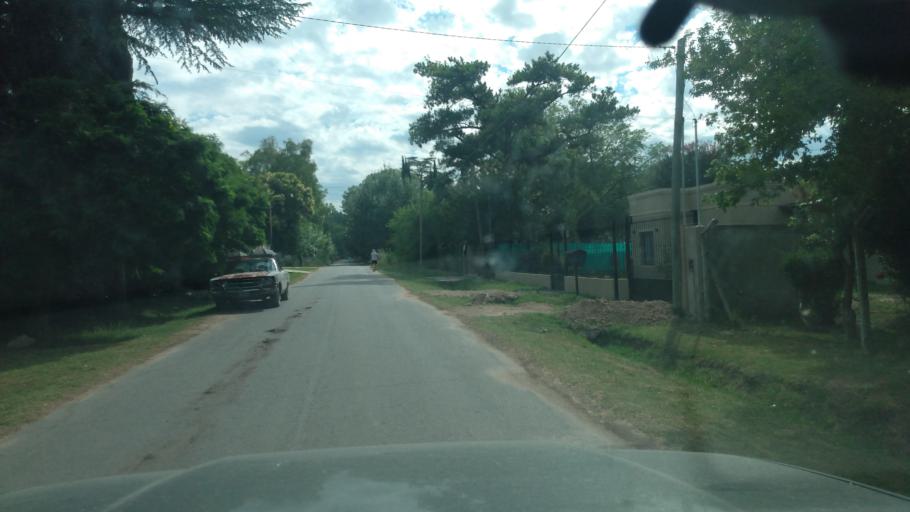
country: AR
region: Buenos Aires
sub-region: Partido de Lujan
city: Lujan
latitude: -34.5917
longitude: -59.0565
